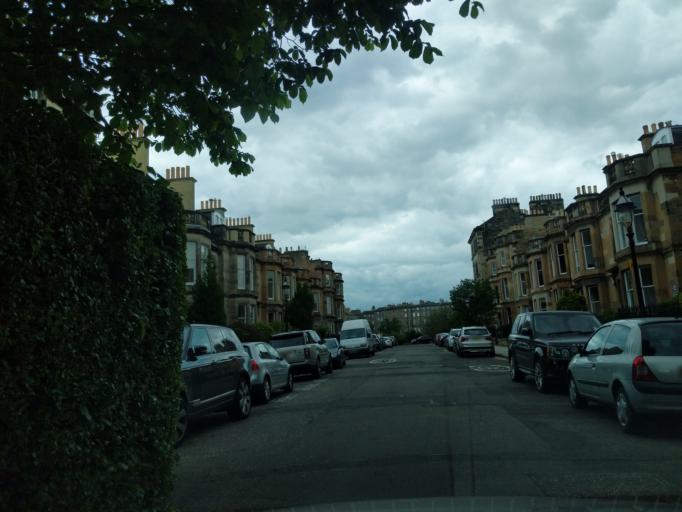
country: GB
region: Scotland
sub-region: Edinburgh
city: Edinburgh
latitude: 55.9559
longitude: -3.2142
